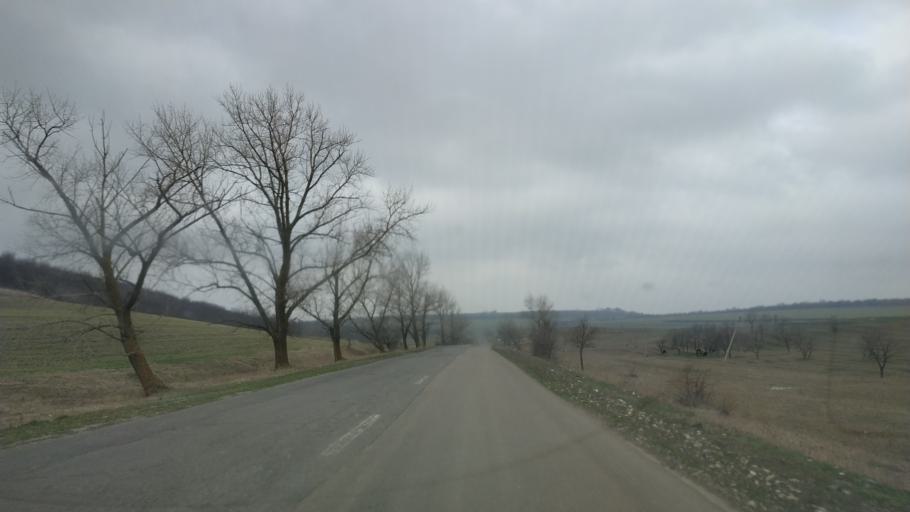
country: MD
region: Gagauzia
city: Bugeac
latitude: 46.3565
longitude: 28.8095
